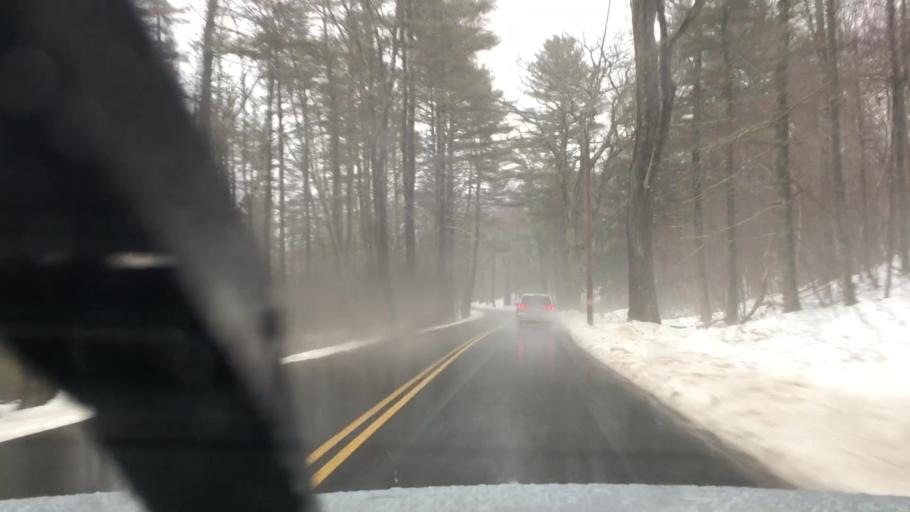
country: US
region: Massachusetts
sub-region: Hampshire County
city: Granby
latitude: 42.2541
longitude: -72.4676
